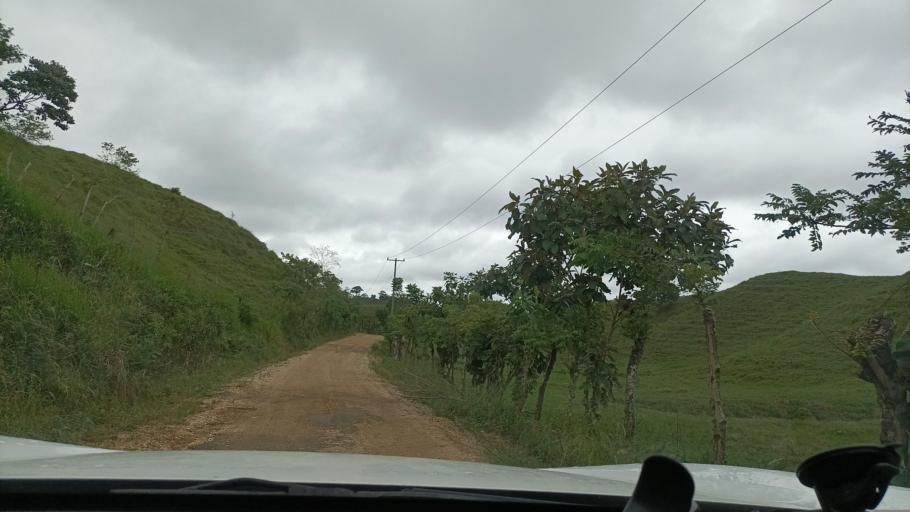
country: MX
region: Veracruz
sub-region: Moloacan
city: Cuichapa
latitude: 17.7901
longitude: -94.3823
